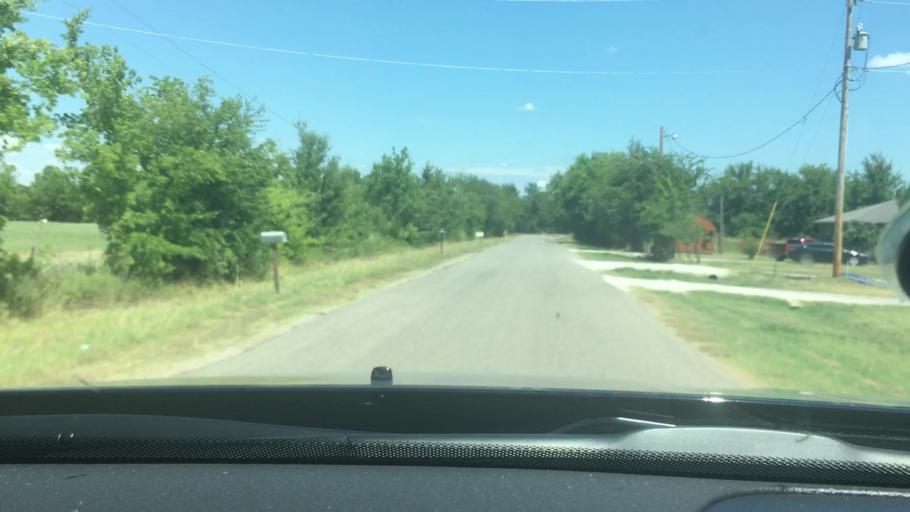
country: US
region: Oklahoma
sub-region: Bryan County
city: Durant
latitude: 33.9928
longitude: -96.2337
